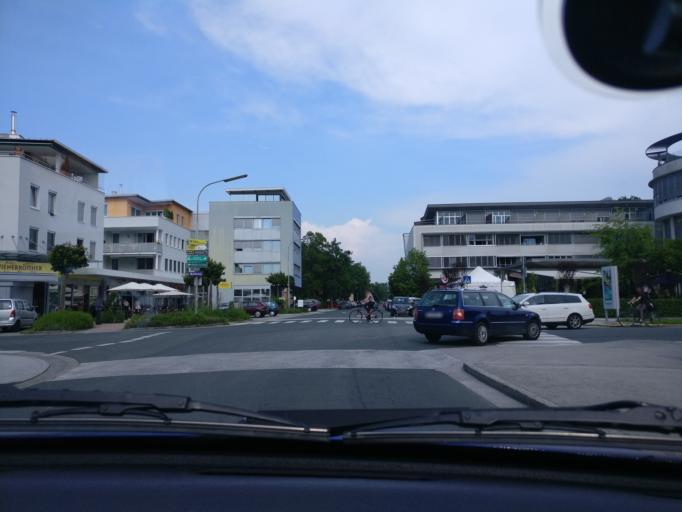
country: AT
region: Carinthia
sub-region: Klagenfurt am Woerthersee
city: Klagenfurt am Woerthersee
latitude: 46.6178
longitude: 14.2671
